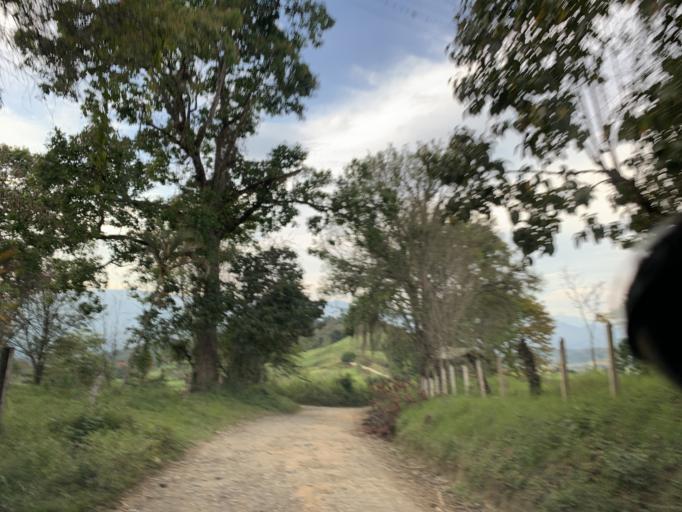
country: CO
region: Boyaca
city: Santana
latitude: 6.0712
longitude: -73.4854
